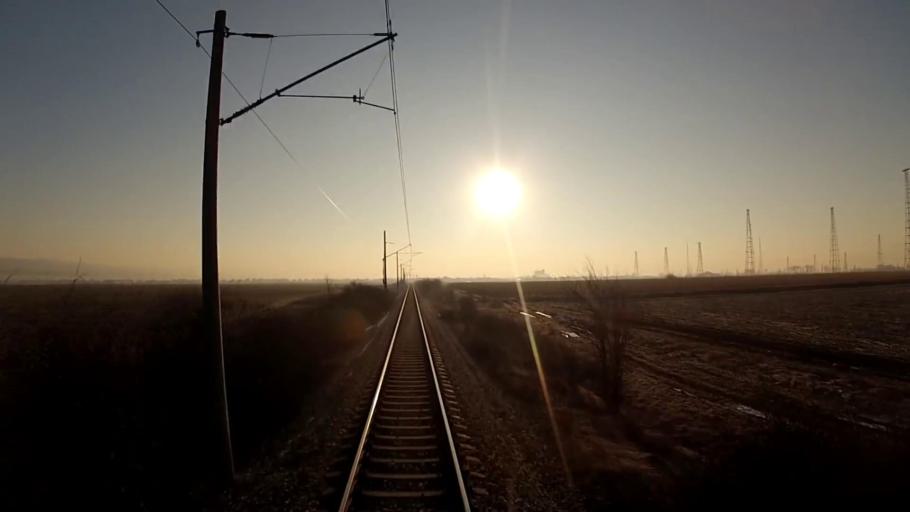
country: BG
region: Sofiya
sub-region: Obshtina Kostinbrod
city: Kostinbrod
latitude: 42.8107
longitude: 23.1938
